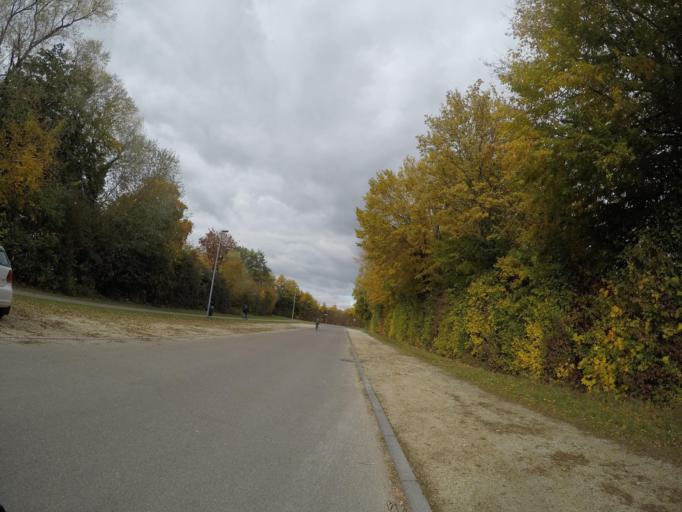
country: DE
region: Baden-Wuerttemberg
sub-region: Tuebingen Region
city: Munderkingen
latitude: 48.2306
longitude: 9.6491
